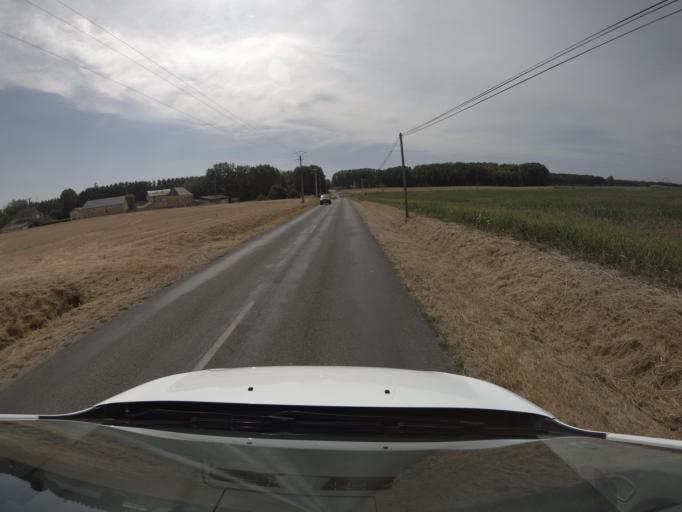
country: FR
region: Poitou-Charentes
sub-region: Departement des Deux-Sevres
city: Saint-Leger-de-Montbrun
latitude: 47.0095
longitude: -0.0696
